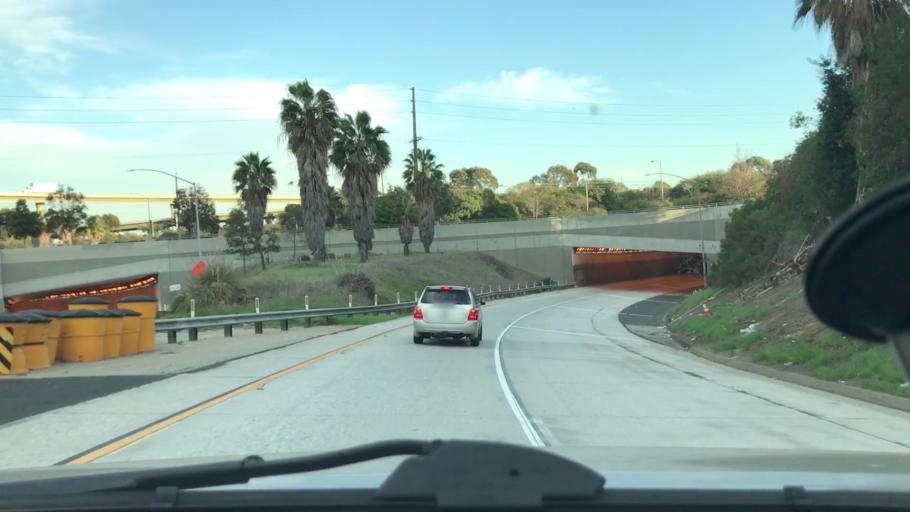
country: US
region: California
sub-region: Los Angeles County
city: Del Aire
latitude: 33.9289
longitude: -118.3713
